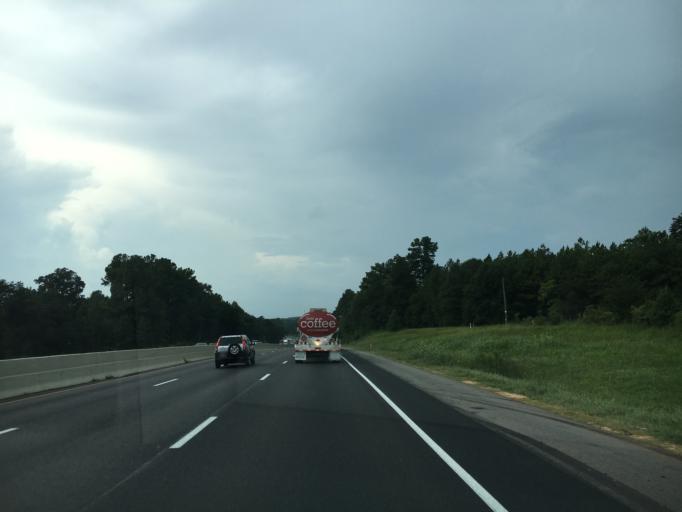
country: US
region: South Carolina
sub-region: Spartanburg County
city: Wellford
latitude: 34.9567
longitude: -82.0613
